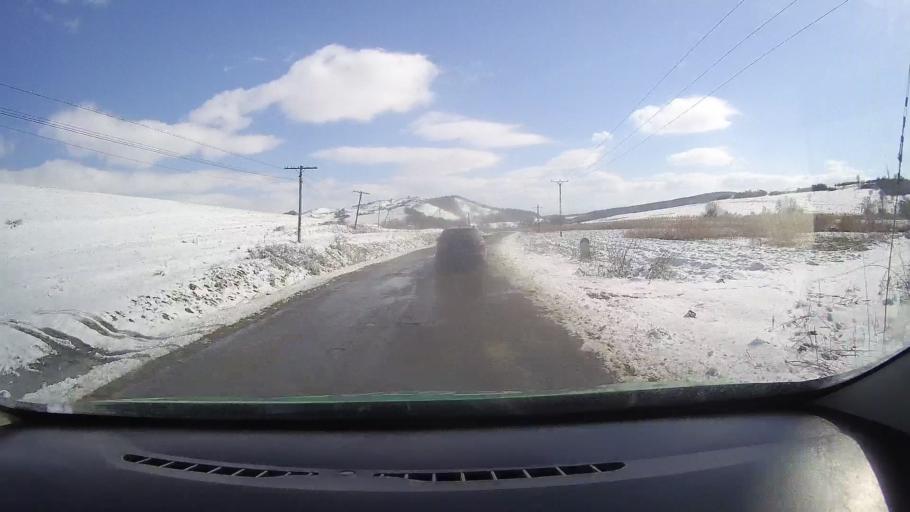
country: RO
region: Sibiu
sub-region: Comuna Altina
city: Altina
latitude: 45.9800
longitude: 24.4613
